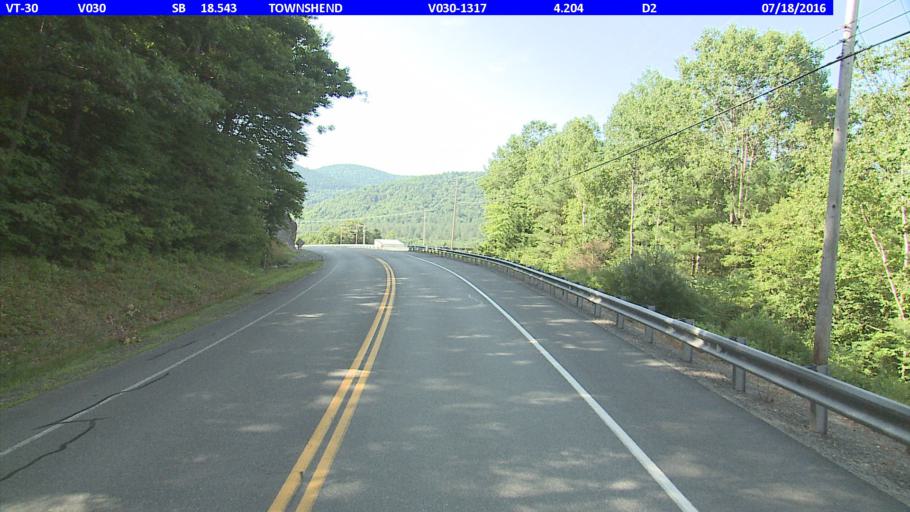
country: US
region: Vermont
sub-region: Windham County
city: Newfane
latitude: 43.0557
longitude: -72.7018
